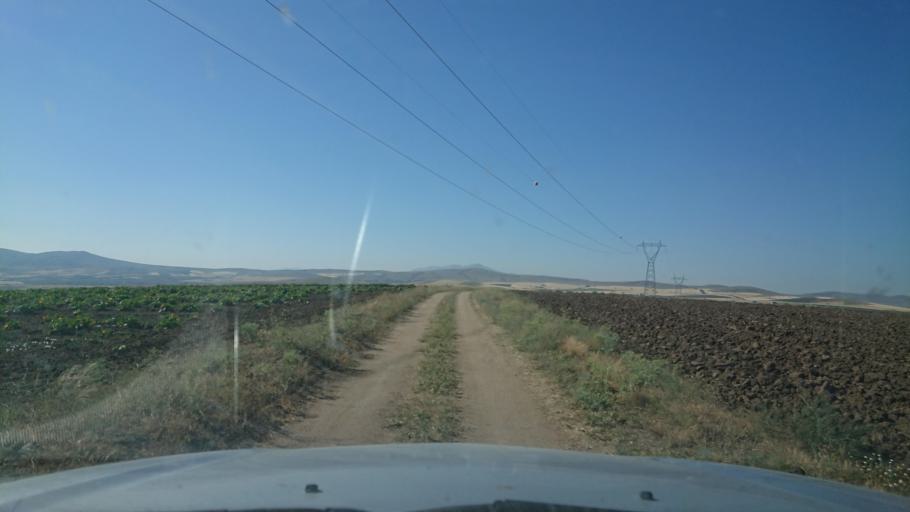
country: TR
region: Aksaray
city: Agacoren
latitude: 38.8366
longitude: 33.9449
